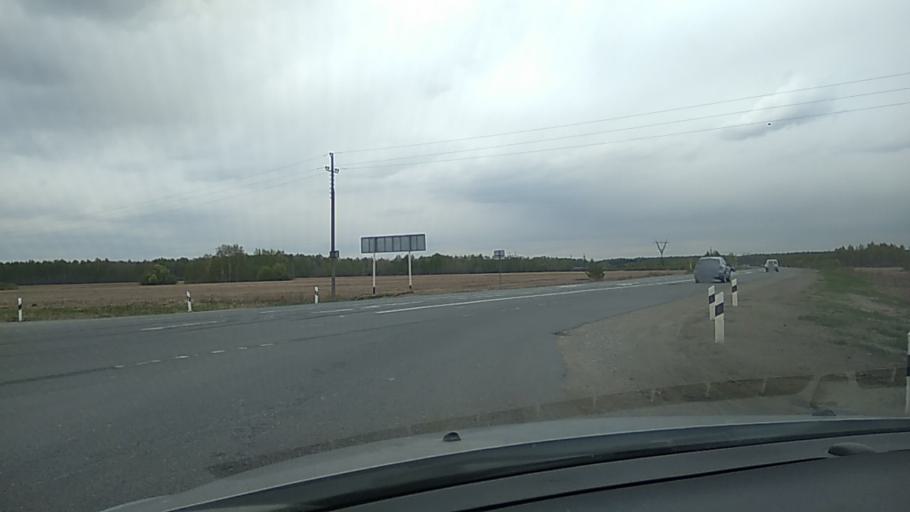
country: RU
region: Sverdlovsk
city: Martyush
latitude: 56.4107
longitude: 61.7864
